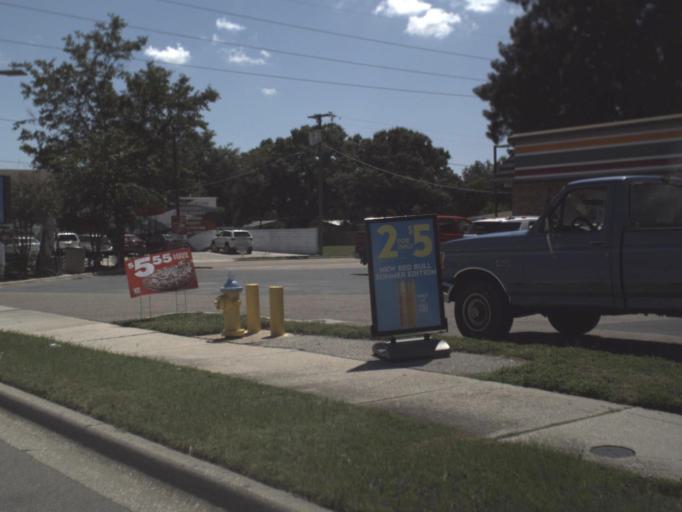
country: US
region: Florida
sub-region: Hillsborough County
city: Tampa
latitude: 27.8844
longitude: -82.5066
